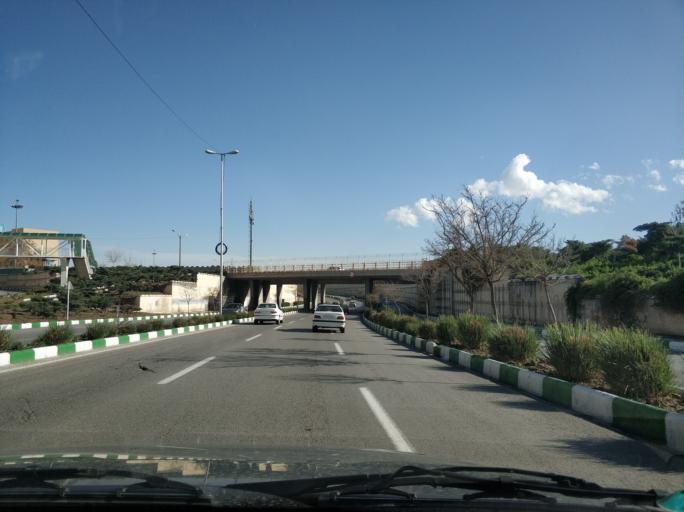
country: IR
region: Razavi Khorasan
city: Mashhad
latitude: 36.3059
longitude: 59.6274
